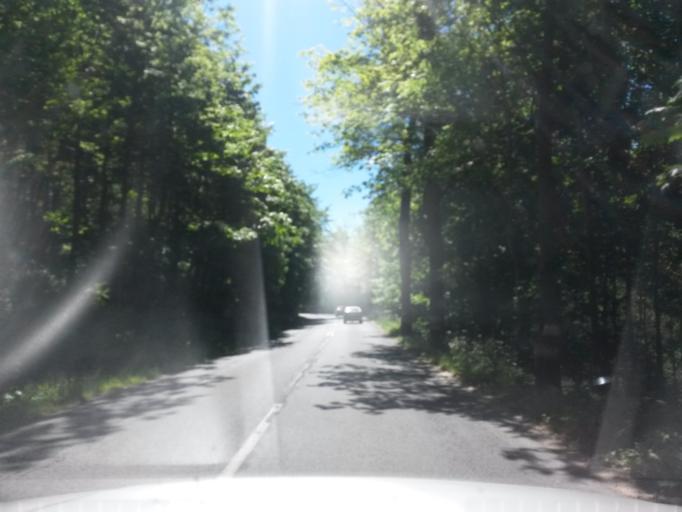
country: PL
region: Lower Silesian Voivodeship
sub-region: Powiat jeleniogorski
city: Kowary
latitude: 50.7686
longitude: 15.8584
